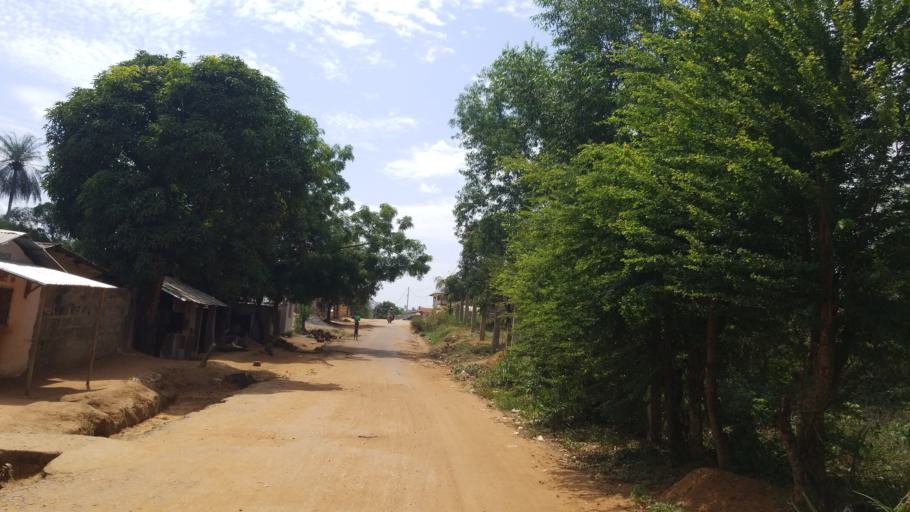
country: SL
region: Western Area
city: Waterloo
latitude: 8.3164
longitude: -13.0576
